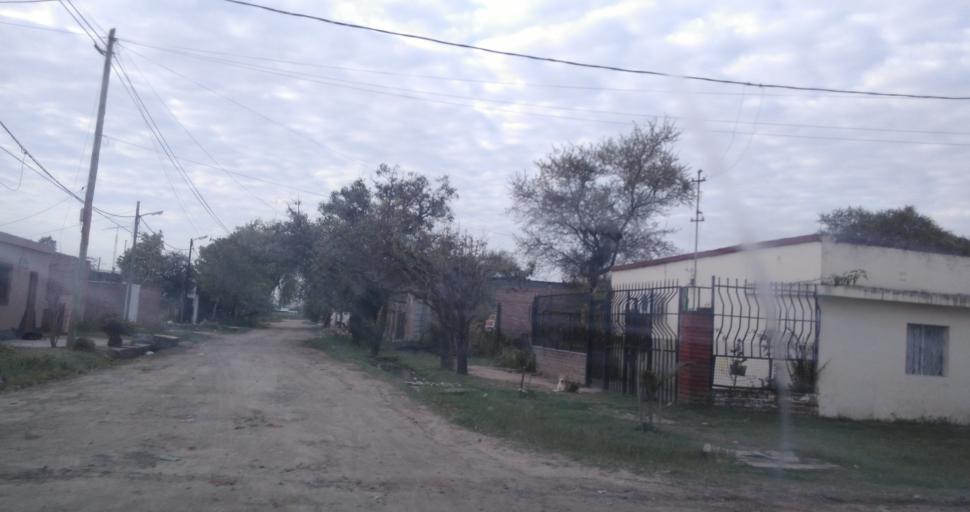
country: AR
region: Chaco
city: Fontana
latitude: -27.4510
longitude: -59.0328
